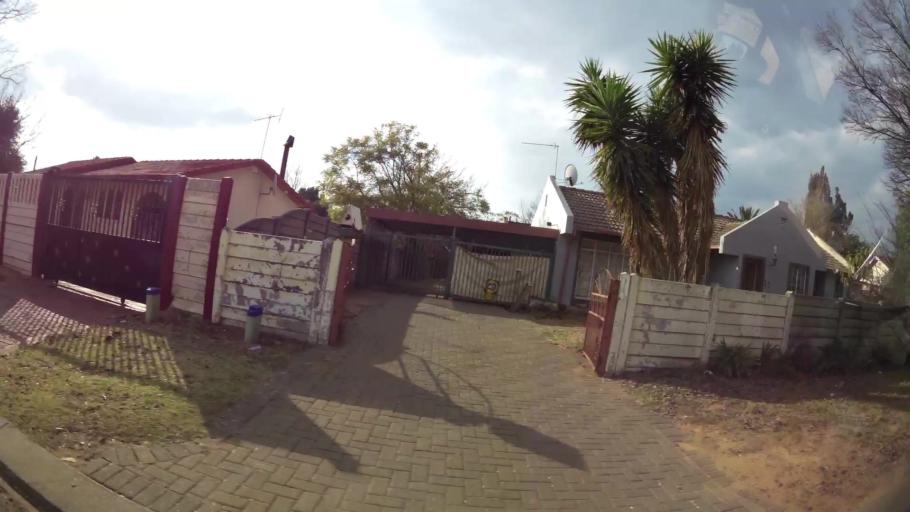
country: ZA
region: Gauteng
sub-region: Ekurhuleni Metropolitan Municipality
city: Benoni
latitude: -26.1205
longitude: 28.3732
